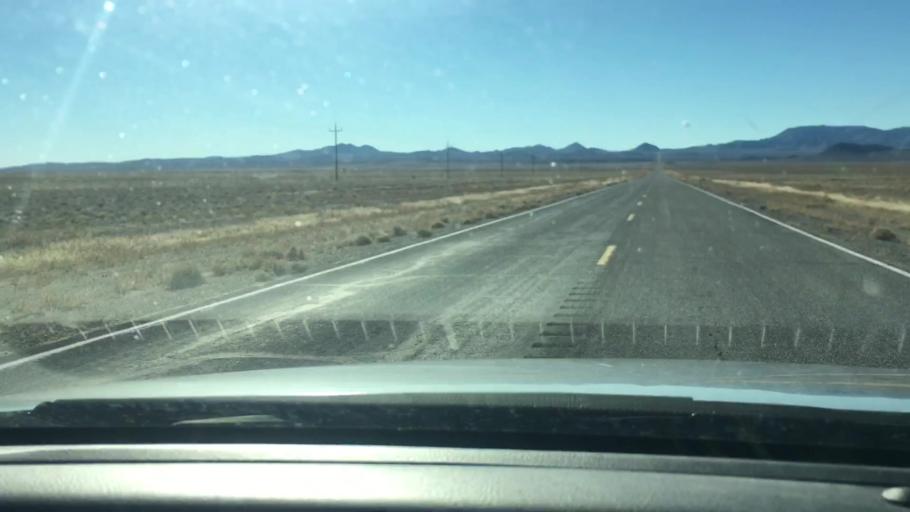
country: US
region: Nevada
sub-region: Nye County
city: Tonopah
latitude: 38.1528
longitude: -116.5554
